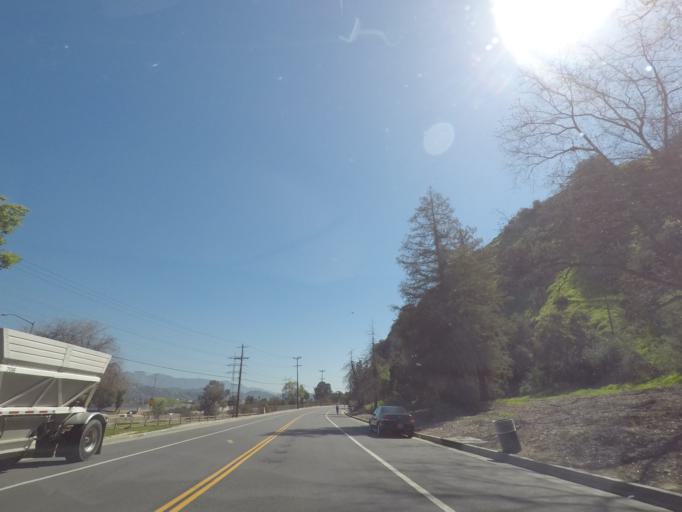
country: US
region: California
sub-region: Los Angeles County
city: Burbank
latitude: 34.1550
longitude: -118.2966
